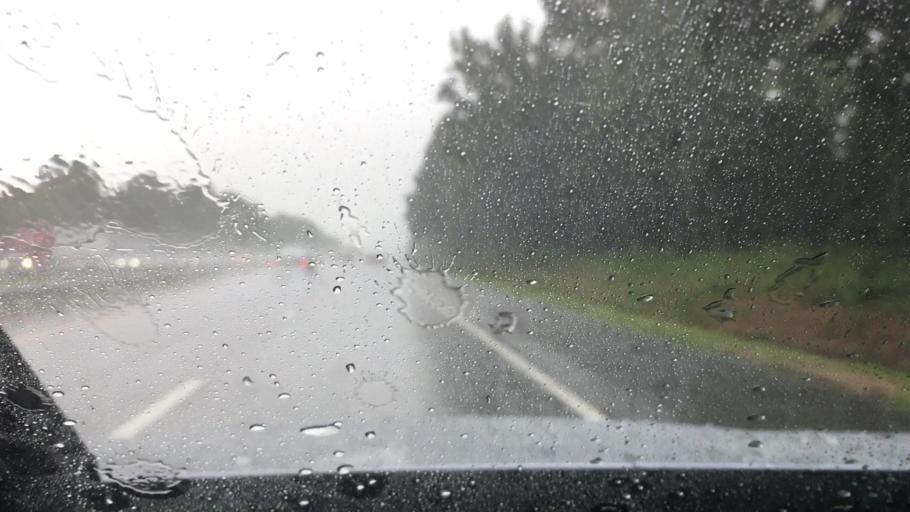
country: US
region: North Carolina
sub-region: Halifax County
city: Halifax
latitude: 36.3492
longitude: -77.6837
